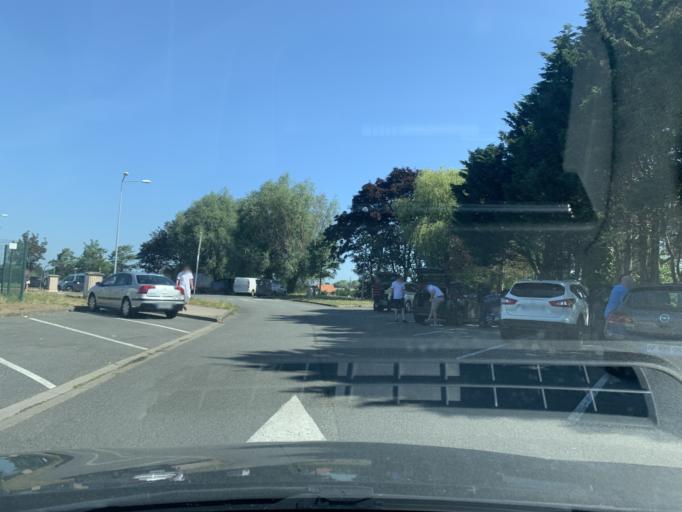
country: FR
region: Nord-Pas-de-Calais
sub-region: Departement du Nord
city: Steenvoorde
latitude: 50.8259
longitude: 2.5863
